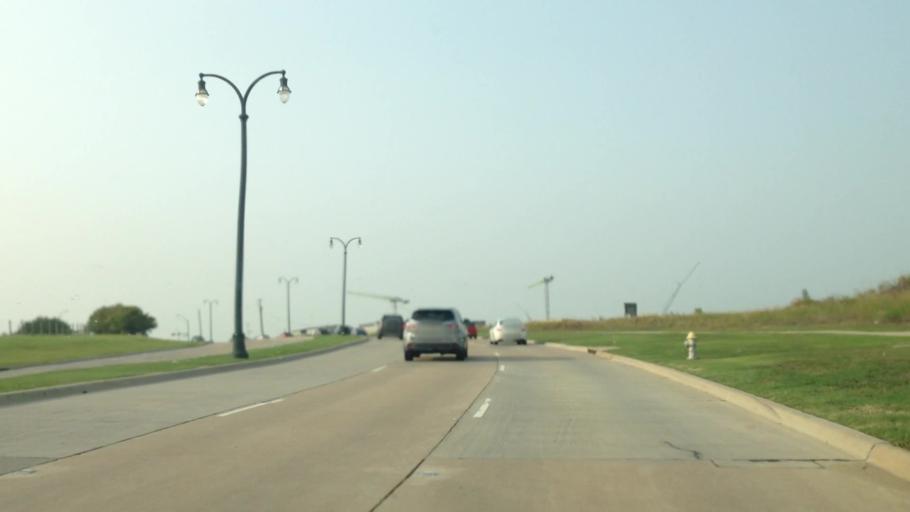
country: US
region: Texas
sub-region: Denton County
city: The Colony
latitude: 33.0652
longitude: -96.8613
